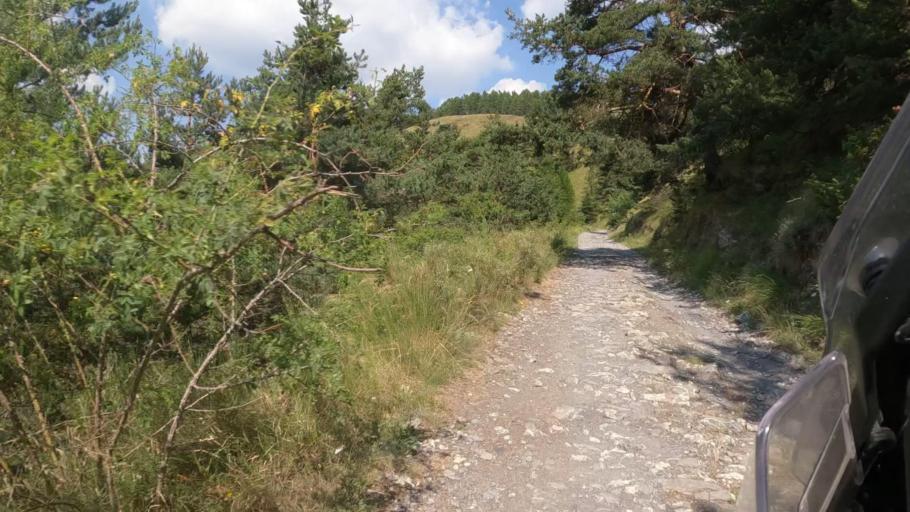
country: IT
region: Piedmont
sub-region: Provincia di Cuneo
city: Briga Alta
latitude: 44.0397
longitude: 7.7005
